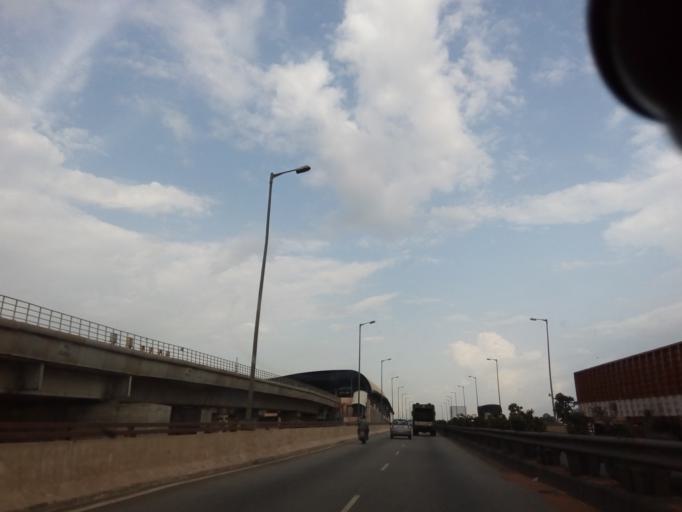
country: IN
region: Karnataka
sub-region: Bangalore Urban
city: Bangalore
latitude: 13.0371
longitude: 77.5235
